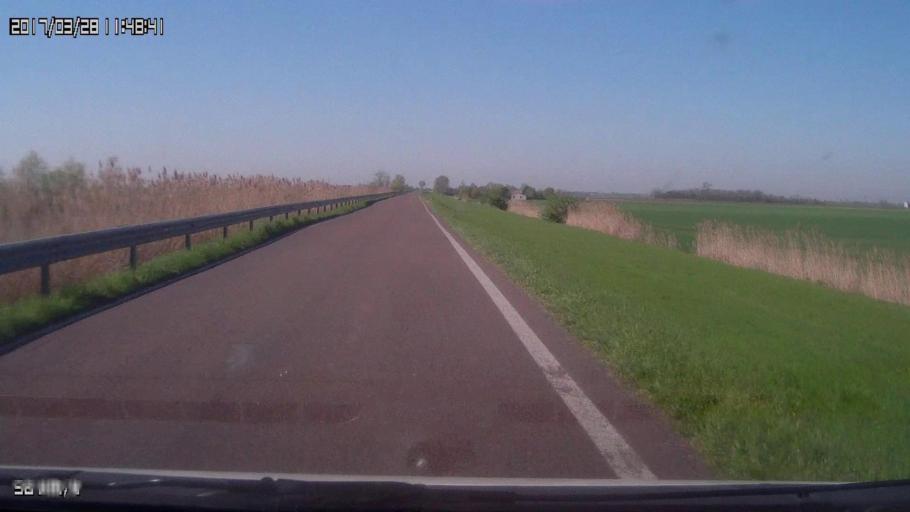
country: IT
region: Veneto
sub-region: Provincia di Venezia
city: Sant'Anna
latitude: 45.1604
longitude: 12.2203
